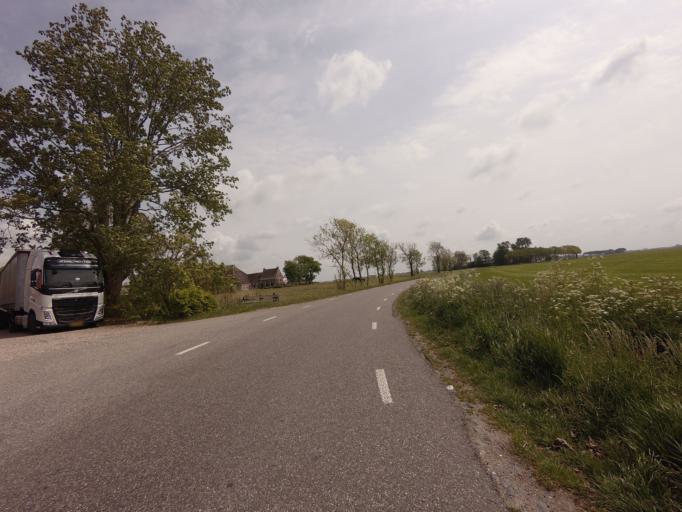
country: NL
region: Friesland
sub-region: Sudwest Fryslan
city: Bolsward
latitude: 53.1118
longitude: 5.4891
